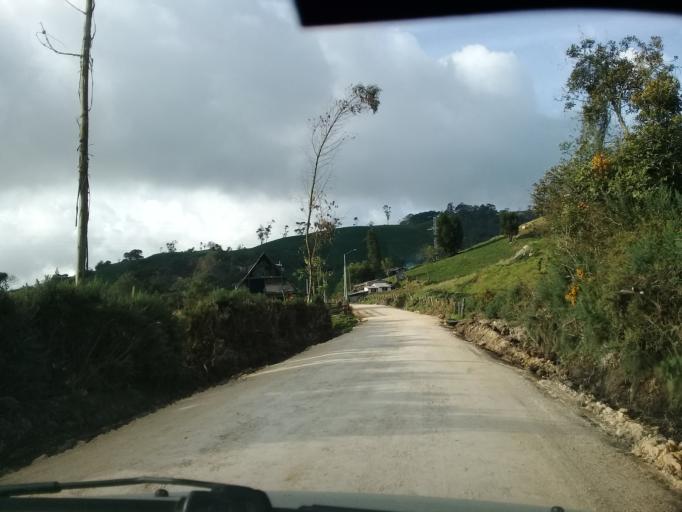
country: CO
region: Cundinamarca
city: Sibate
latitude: 4.4324
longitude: -74.2866
